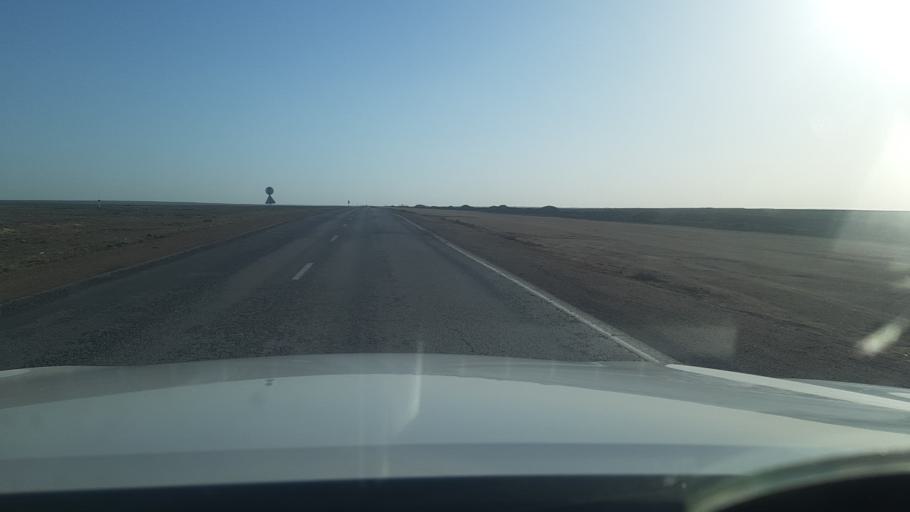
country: KZ
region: Qaraghandy
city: Saryshaghan
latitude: 46.4336
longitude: 73.9596
